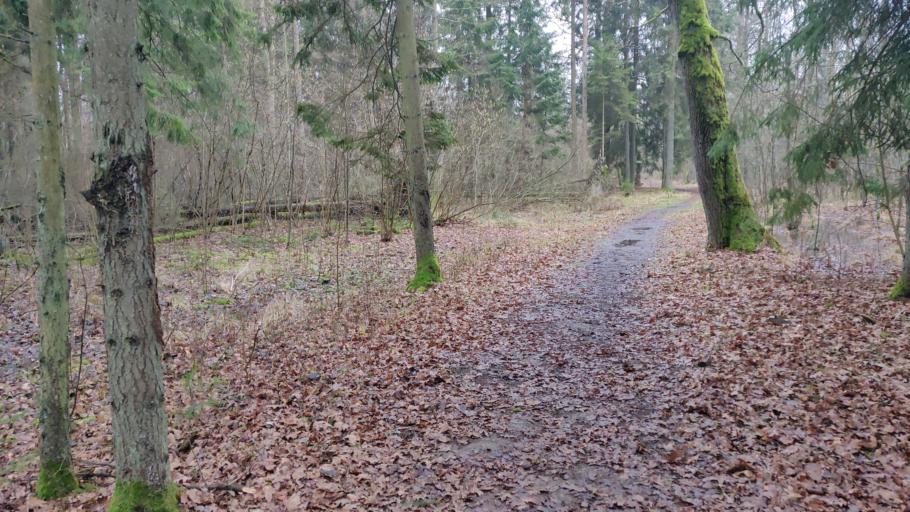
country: LT
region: Vilnius County
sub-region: Vilniaus Rajonas
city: Vievis
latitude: 54.8355
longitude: 24.9541
